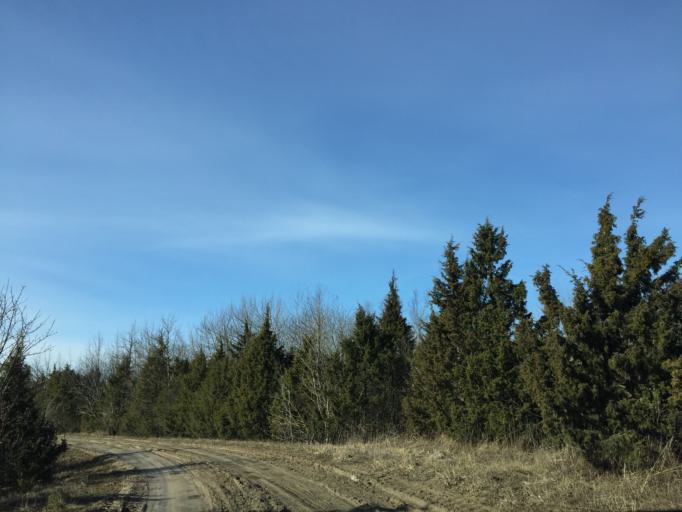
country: EE
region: Laeaene
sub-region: Haapsalu linn
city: Haapsalu
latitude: 58.6606
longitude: 23.5158
